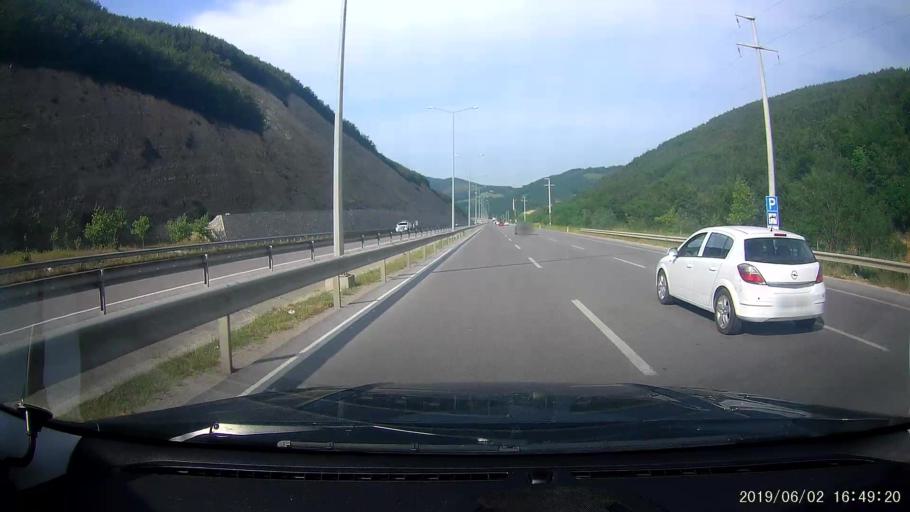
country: TR
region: Samsun
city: Taflan
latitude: 41.2361
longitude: 36.1594
